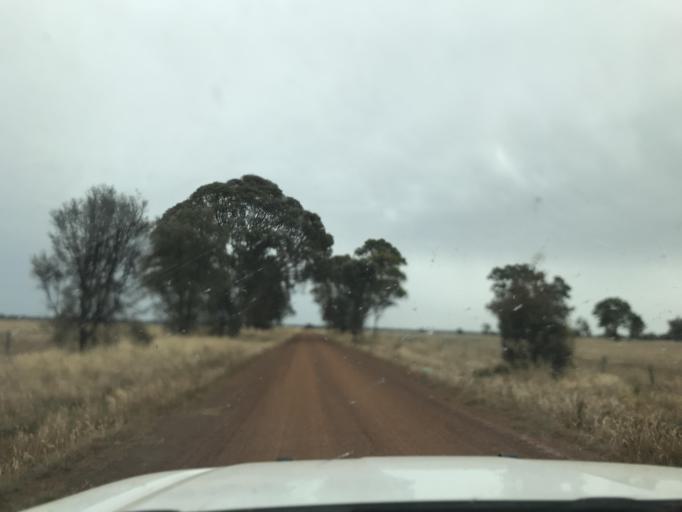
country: AU
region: Victoria
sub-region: Horsham
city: Horsham
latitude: -37.0612
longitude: 141.6172
